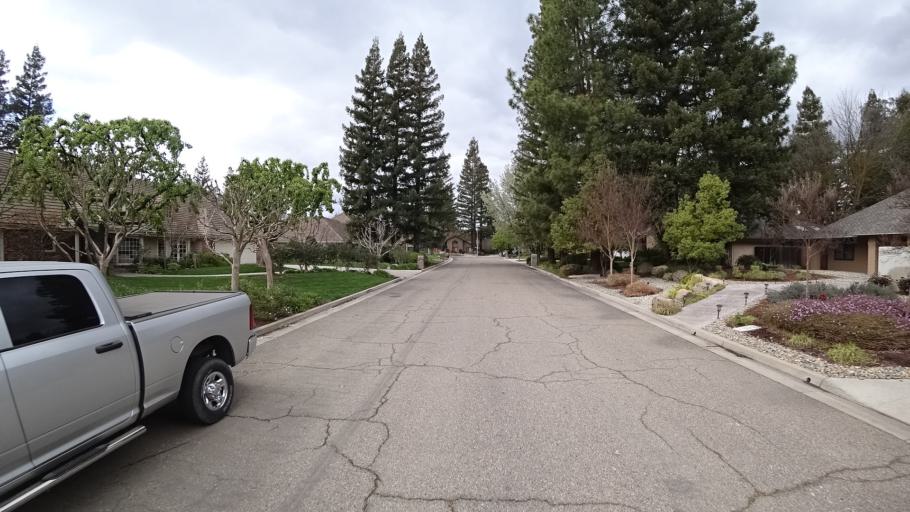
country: US
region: California
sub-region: Fresno County
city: Fresno
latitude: 36.8464
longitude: -119.8461
